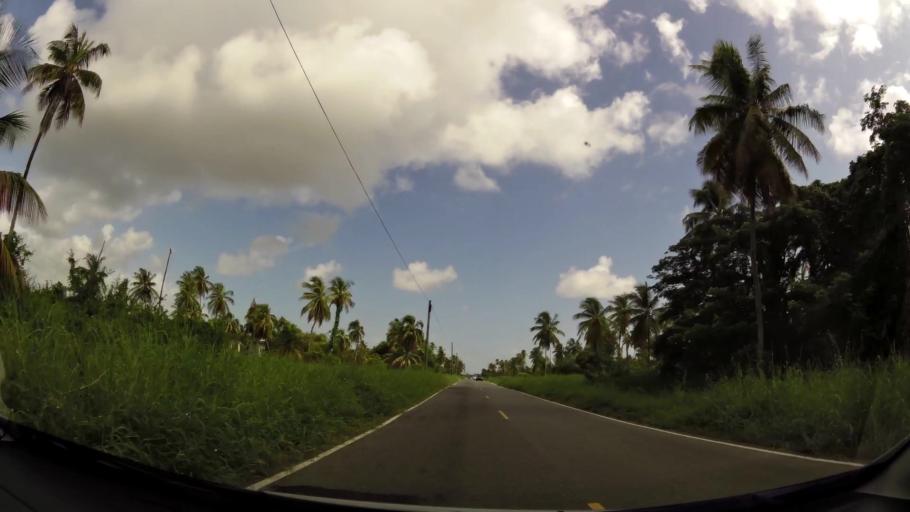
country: GY
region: Demerara-Mahaica
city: Mahaica Village
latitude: 6.7232
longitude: -57.9369
